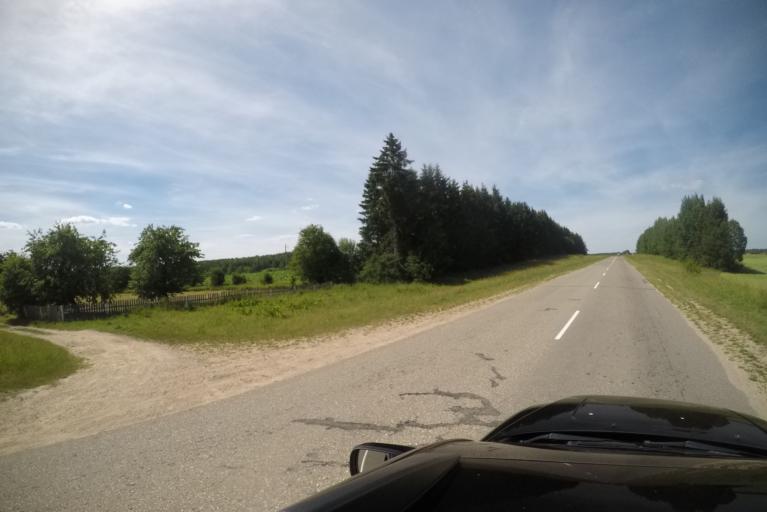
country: BY
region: Grodnenskaya
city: Hal'shany
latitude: 54.2665
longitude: 25.9931
